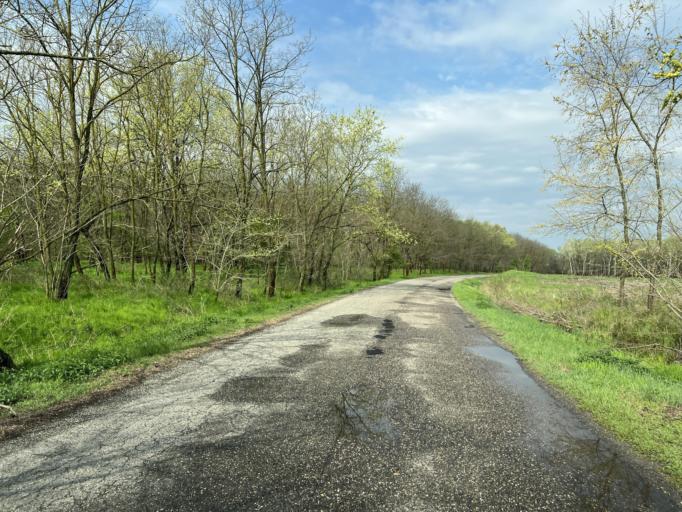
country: HU
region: Pest
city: Hernad
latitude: 47.1710
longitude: 19.4906
